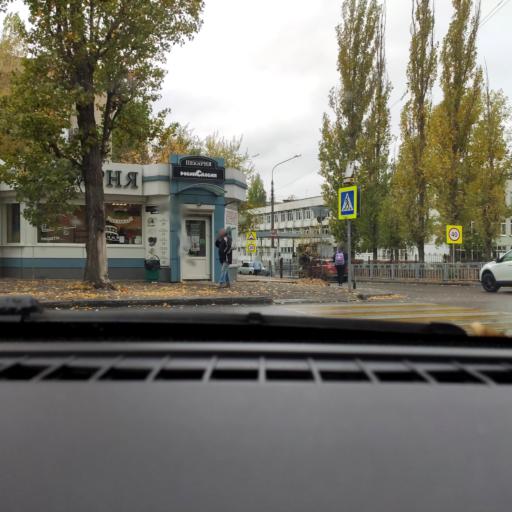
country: RU
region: Voronezj
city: Voronezh
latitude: 51.6898
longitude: 39.2604
